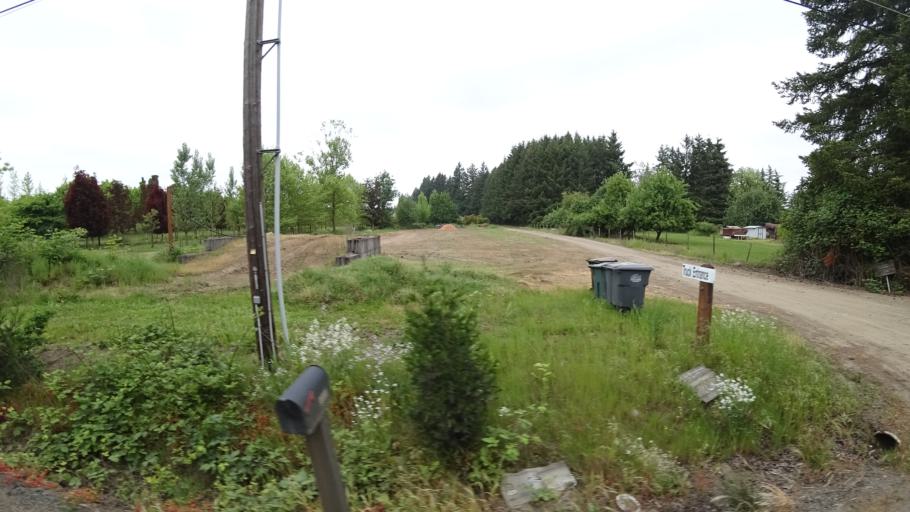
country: US
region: Oregon
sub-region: Washington County
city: Hillsboro
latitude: 45.4801
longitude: -122.9877
